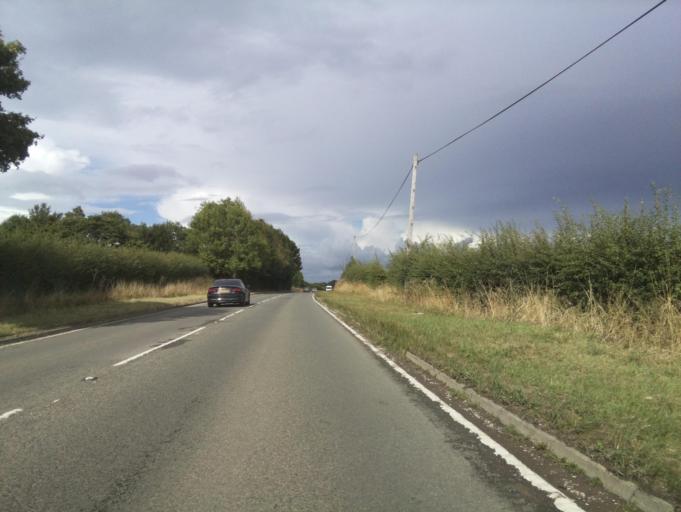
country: GB
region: England
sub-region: Shropshire
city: Shifnal
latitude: 52.6563
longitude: -2.3947
